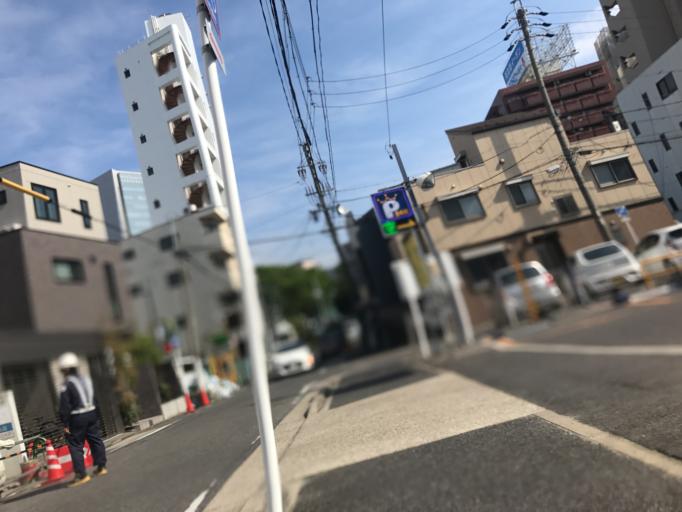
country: JP
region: Aichi
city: Nagoya-shi
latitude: 35.1691
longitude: 136.9313
